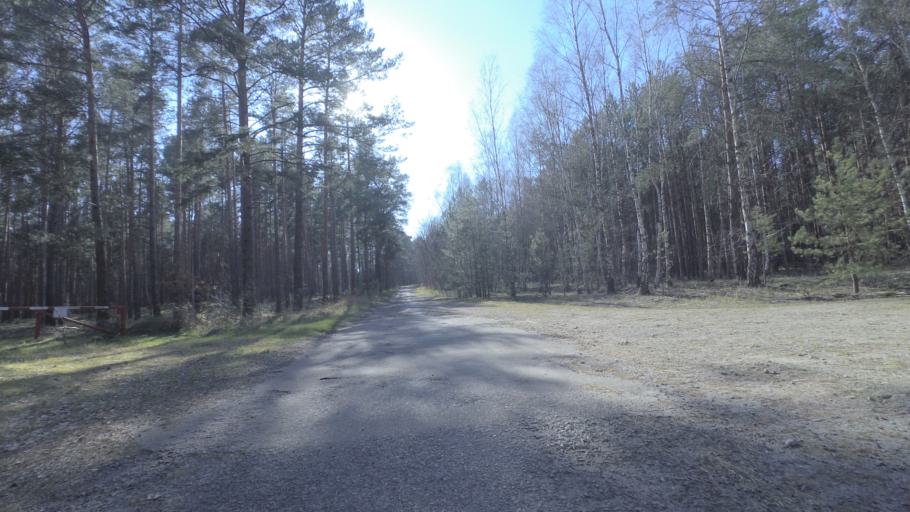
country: DE
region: Brandenburg
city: Teupitz
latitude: 52.1214
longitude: 13.5497
